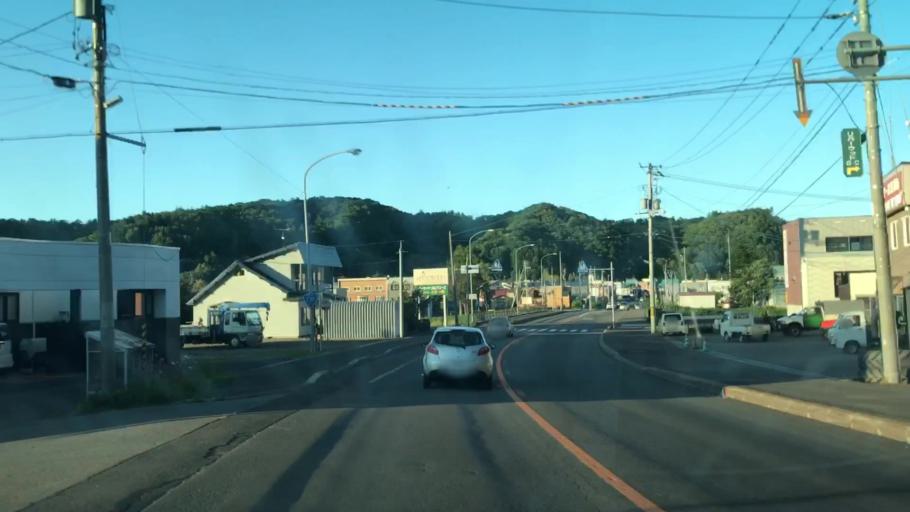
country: JP
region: Hokkaido
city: Niseko Town
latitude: 42.7935
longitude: 140.9357
